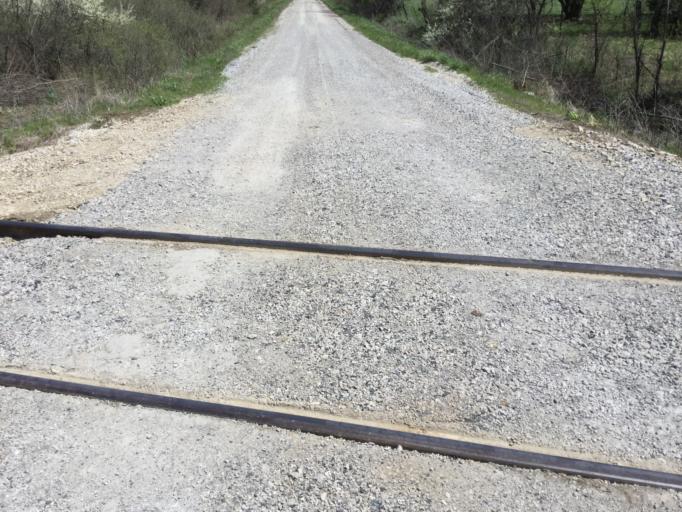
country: US
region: Kansas
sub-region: Montgomery County
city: Cherryvale
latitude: 37.3983
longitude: -95.5034
